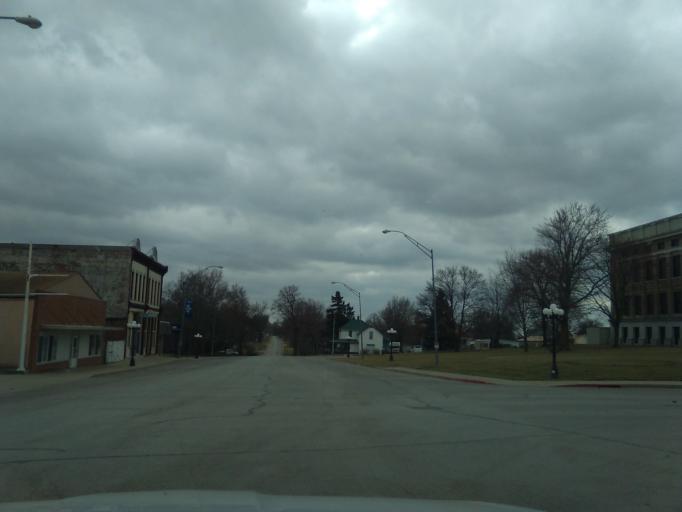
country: US
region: Nebraska
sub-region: Pawnee County
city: Pawnee City
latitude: 40.1086
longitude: -96.1531
